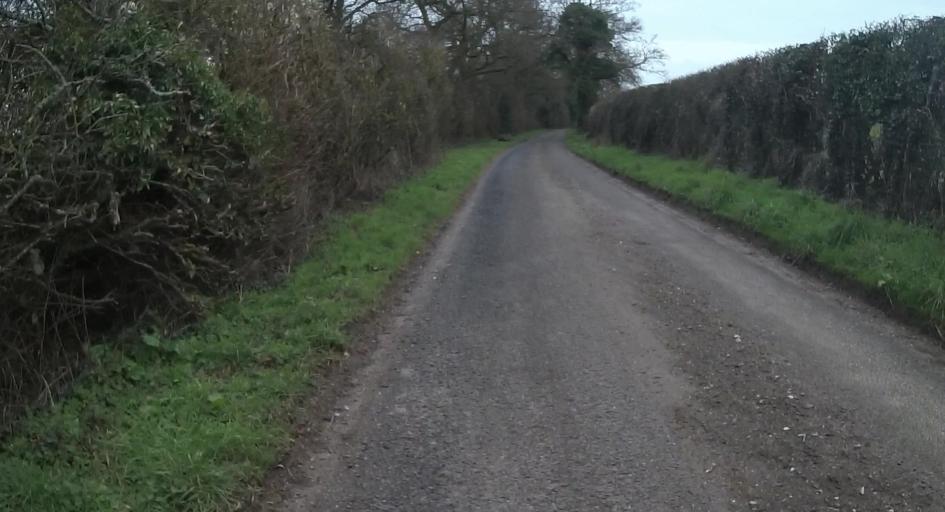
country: GB
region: England
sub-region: Hampshire
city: Overton
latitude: 51.2728
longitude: -1.2521
